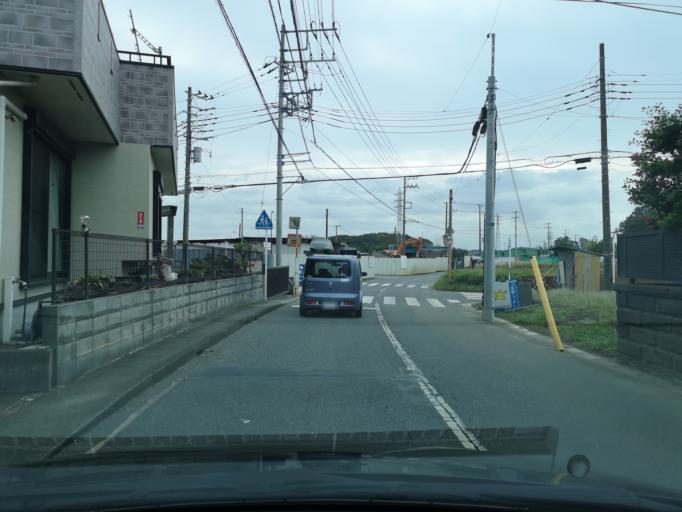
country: JP
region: Kanagawa
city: Atsugi
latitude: 35.3895
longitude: 139.3908
